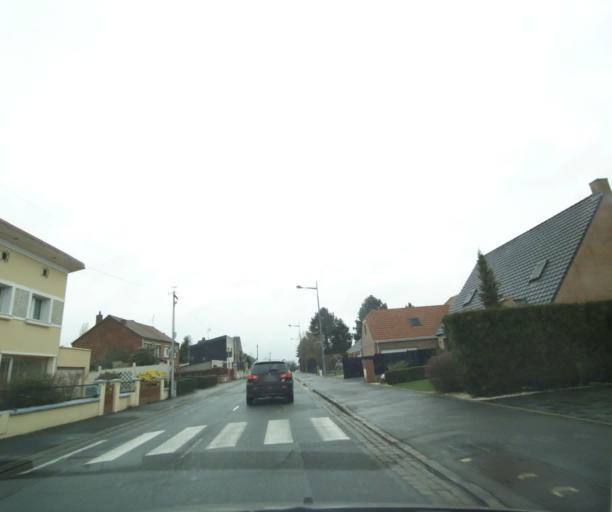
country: FR
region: Nord-Pas-de-Calais
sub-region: Departement du Nord
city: Prouvy
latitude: 50.3233
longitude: 3.4524
